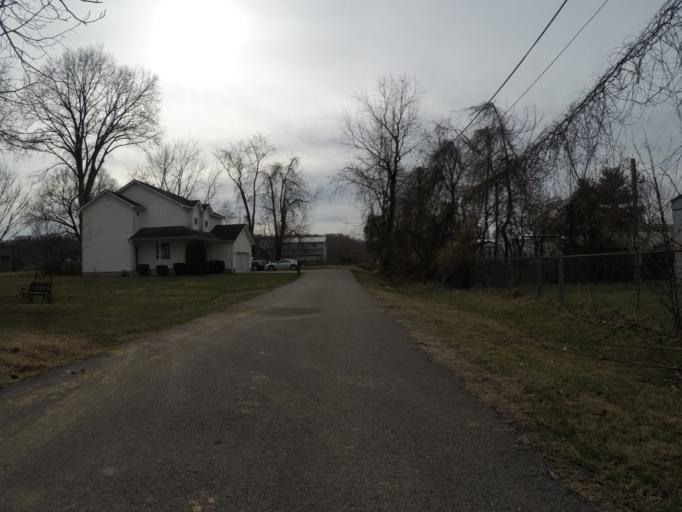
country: US
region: West Virginia
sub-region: Cabell County
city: Pea Ridge
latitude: 38.4459
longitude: -82.3543
